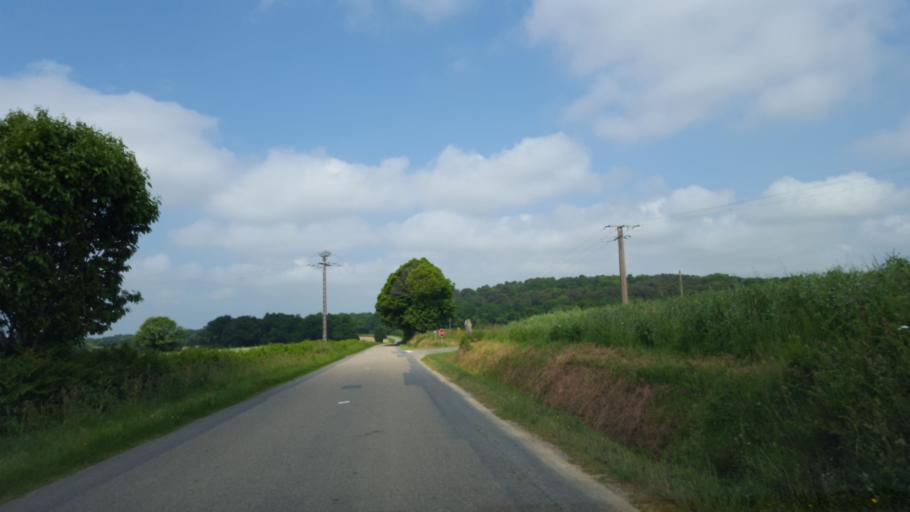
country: FR
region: Brittany
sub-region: Departement d'Ille-et-Vilaine
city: Guignen
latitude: 47.9251
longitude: -1.8892
